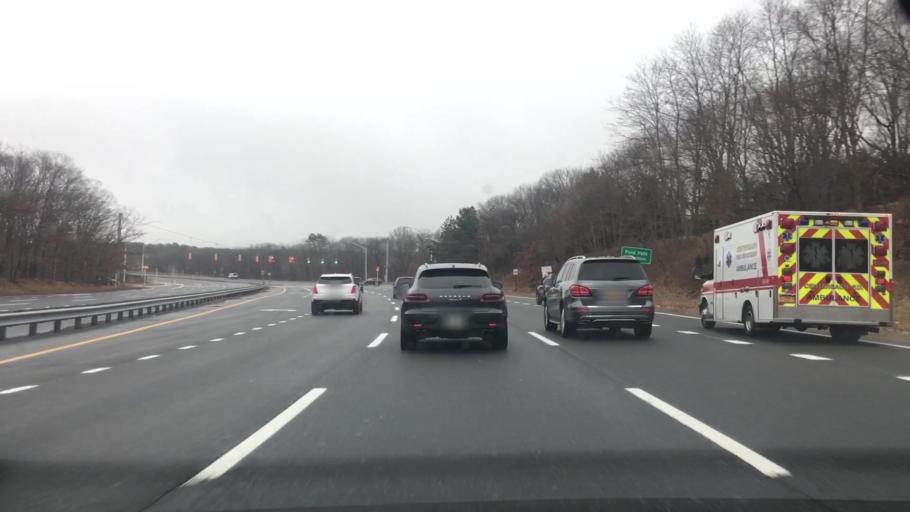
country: US
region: New York
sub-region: Suffolk County
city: Centereach
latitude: 40.8817
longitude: -73.1057
